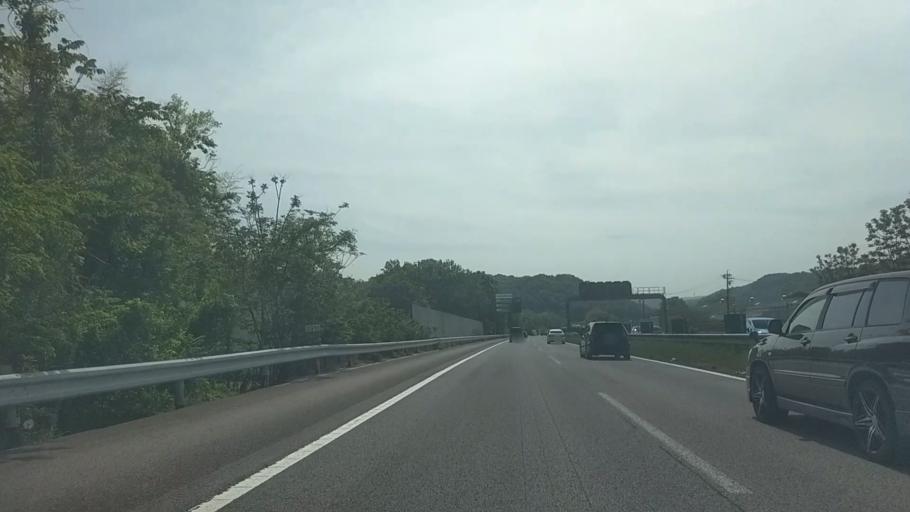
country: JP
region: Aichi
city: Okazaki
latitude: 34.9353
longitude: 137.2135
